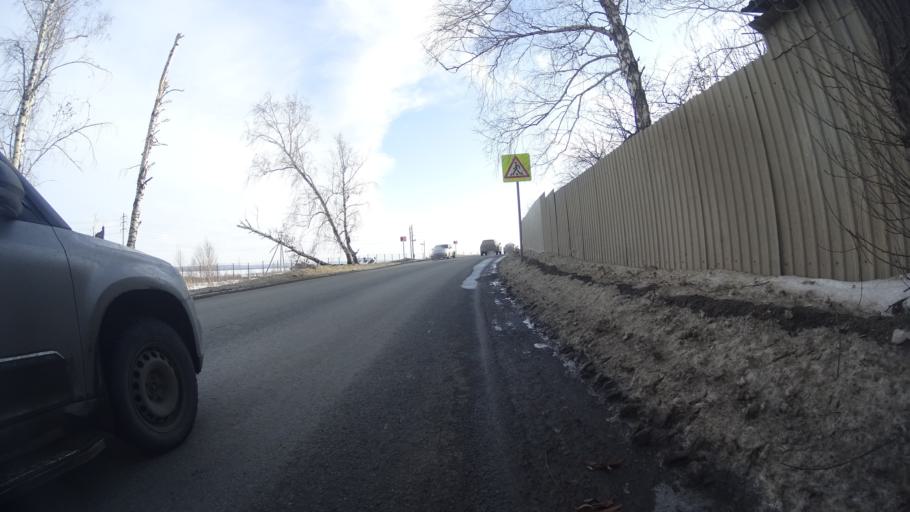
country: RU
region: Chelyabinsk
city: Sargazy
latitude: 55.1252
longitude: 61.2896
